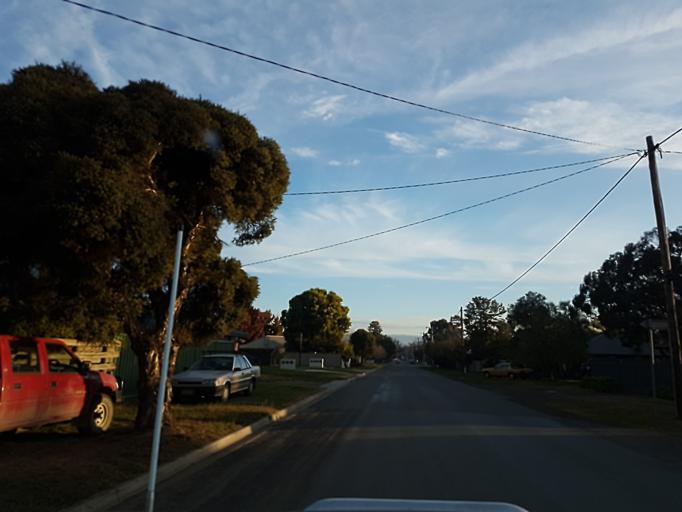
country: AU
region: Victoria
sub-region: Murrindindi
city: Alexandra
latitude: -37.1837
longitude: 145.7119
